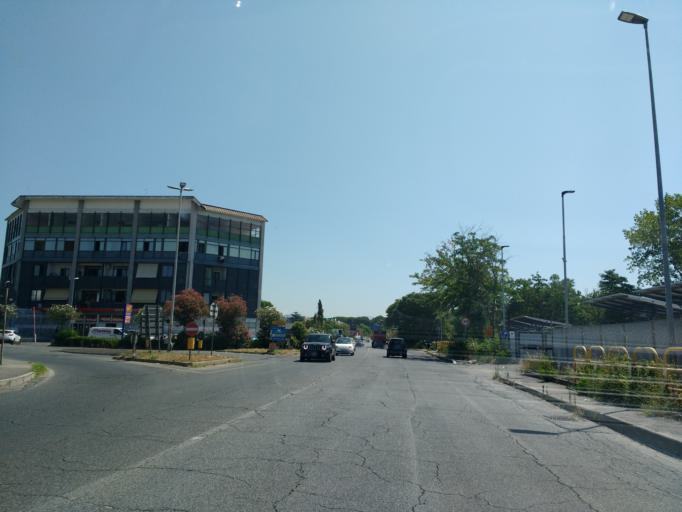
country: IT
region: Latium
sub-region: Citta metropolitana di Roma Capitale
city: Albuccione
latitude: 41.9519
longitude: 12.6916
